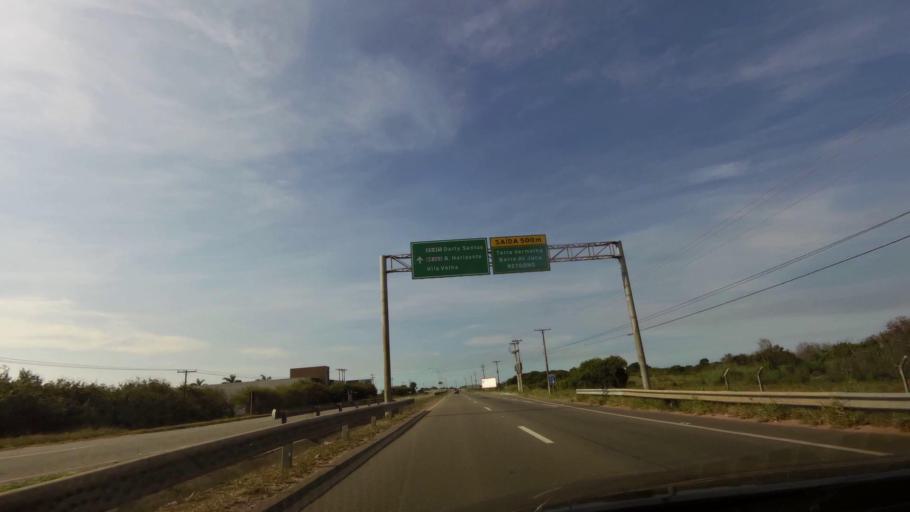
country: BR
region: Espirito Santo
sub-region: Vila Velha
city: Vila Velha
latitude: -20.4543
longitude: -40.3380
